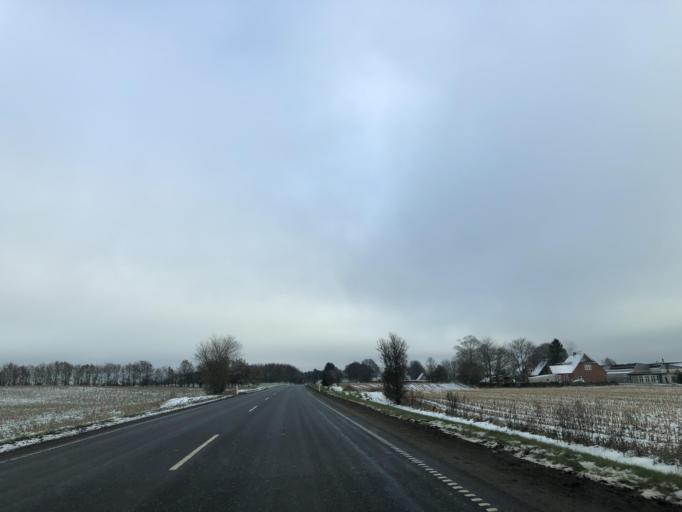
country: DK
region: Central Jutland
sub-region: Horsens Kommune
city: Braedstrup
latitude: 55.8947
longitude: 9.6973
